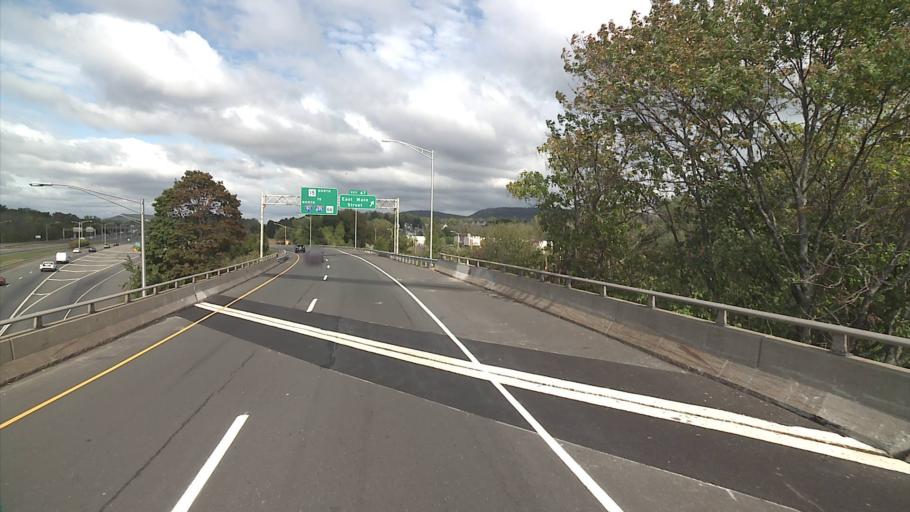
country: US
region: Connecticut
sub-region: New Haven County
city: Meriden
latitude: 41.5209
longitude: -72.7712
